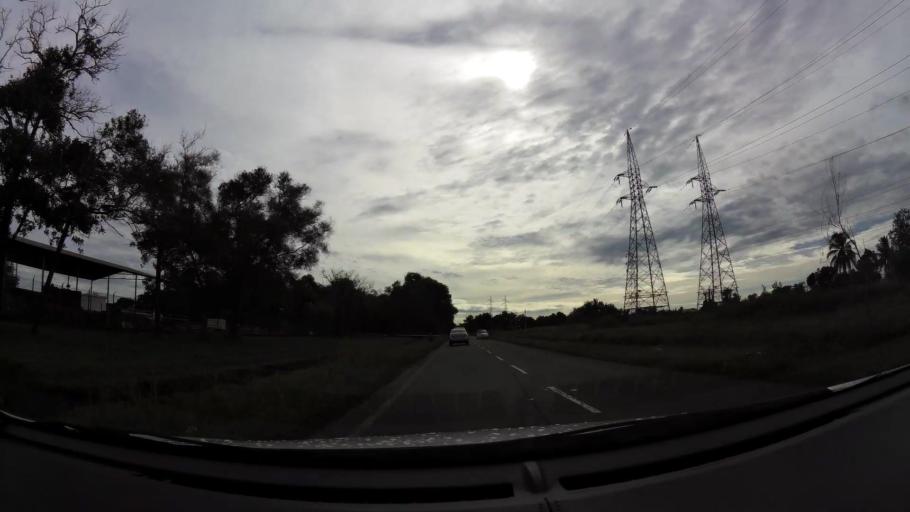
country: BN
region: Belait
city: Seria
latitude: 4.6168
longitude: 114.3450
